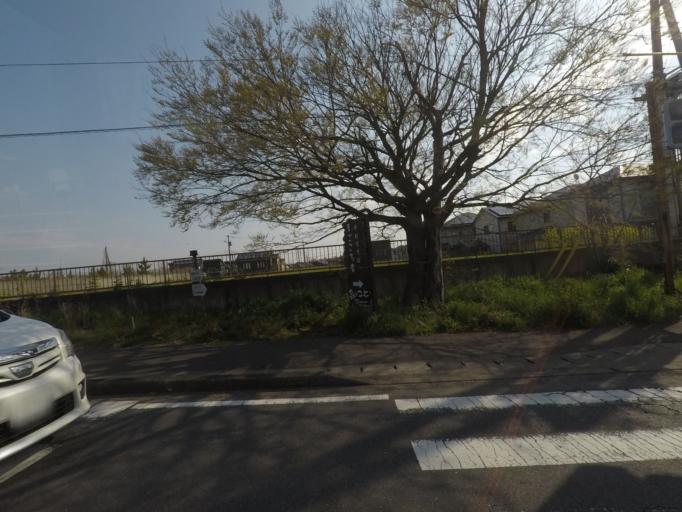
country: JP
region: Chiba
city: Narita
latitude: 35.7533
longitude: 140.3043
